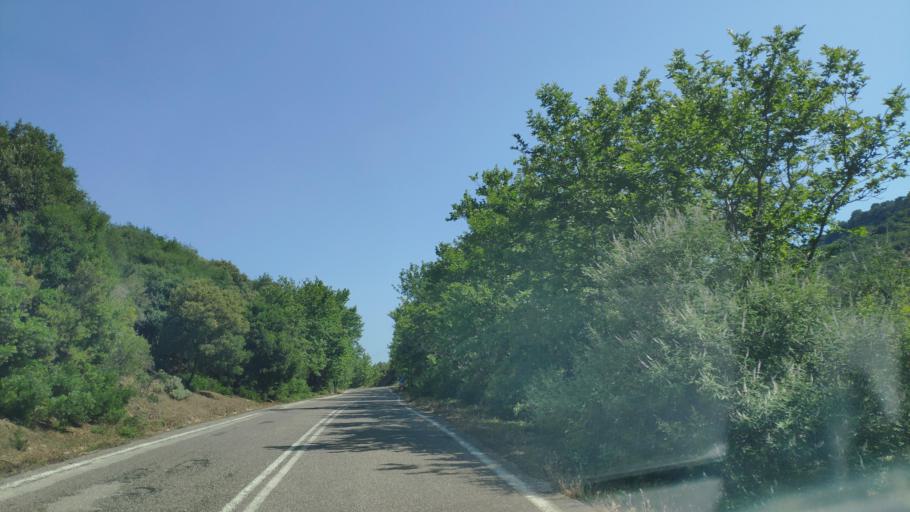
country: GR
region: West Greece
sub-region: Nomos Aitolias kai Akarnanias
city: Lepenou
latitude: 38.7855
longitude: 21.3338
